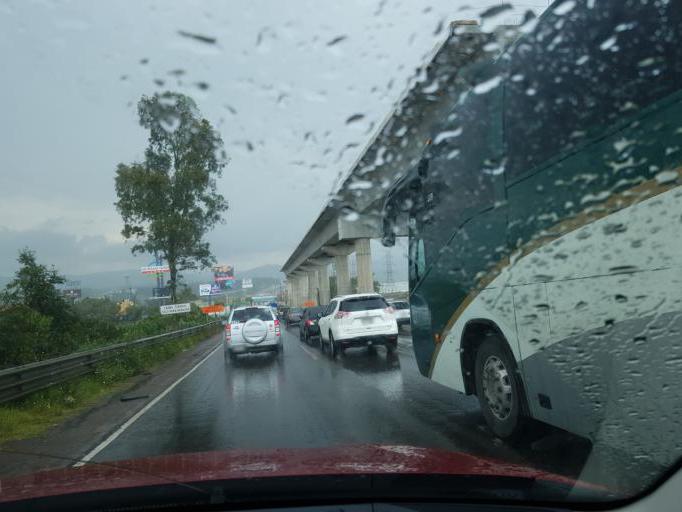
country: MX
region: Mexico
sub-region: Ocoyoacac
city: San Antonio el Llanito
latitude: 19.2808
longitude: -99.4997
